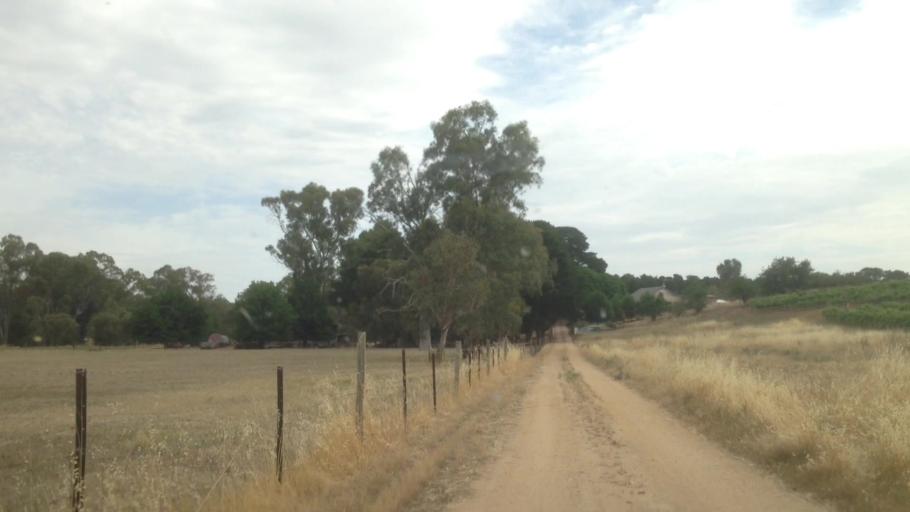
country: AU
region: South Australia
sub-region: Barossa
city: Williamstown
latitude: -34.6760
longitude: 138.8830
